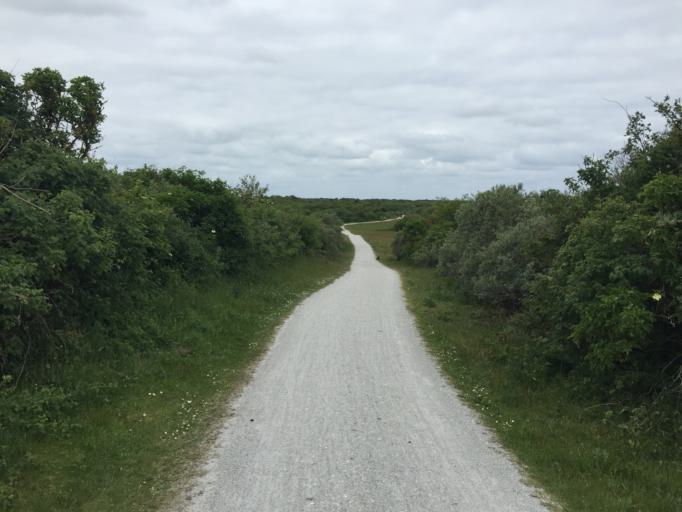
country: NL
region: Friesland
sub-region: Gemeente Schiermonnikoog
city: Schiermonnikoog
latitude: 53.4705
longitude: 6.1487
